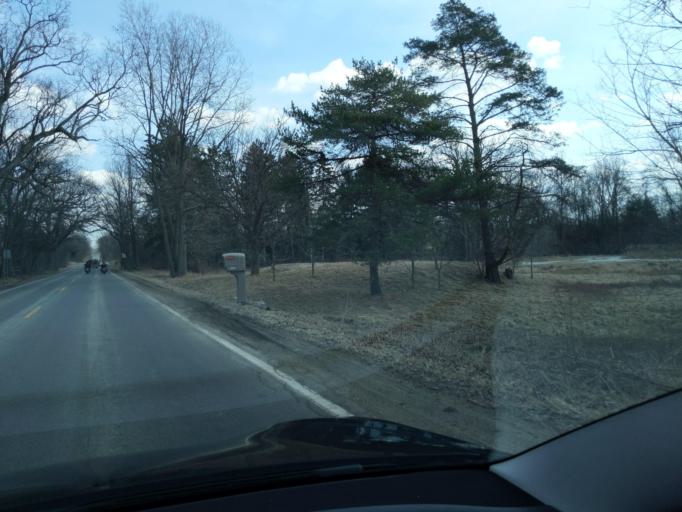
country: US
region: Michigan
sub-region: Livingston County
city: Whitmore Lake
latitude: 42.3805
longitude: -83.7953
